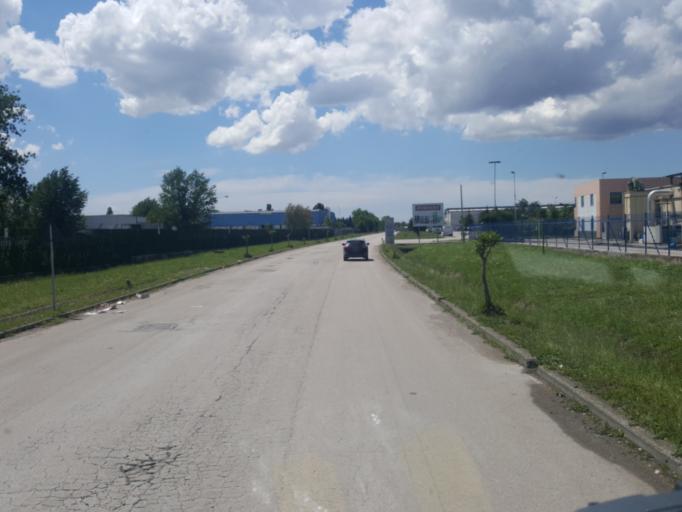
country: IT
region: Campania
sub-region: Provincia di Napoli
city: Pascarola
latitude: 40.9889
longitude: 14.3021
